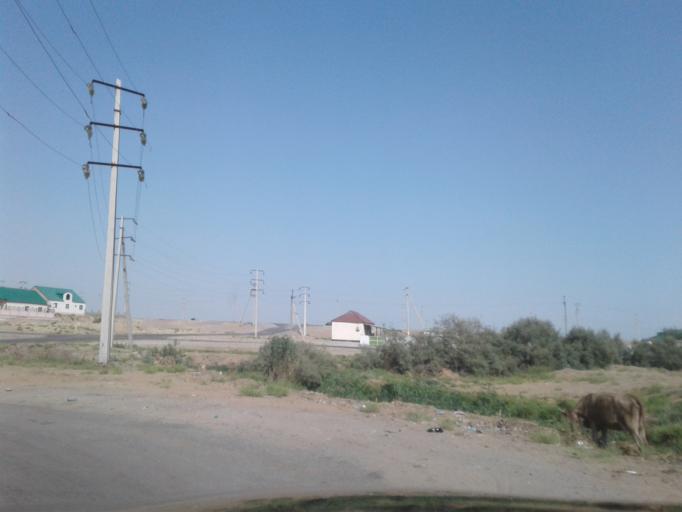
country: TM
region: Ahal
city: Ashgabat
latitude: 37.9718
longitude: 58.4380
